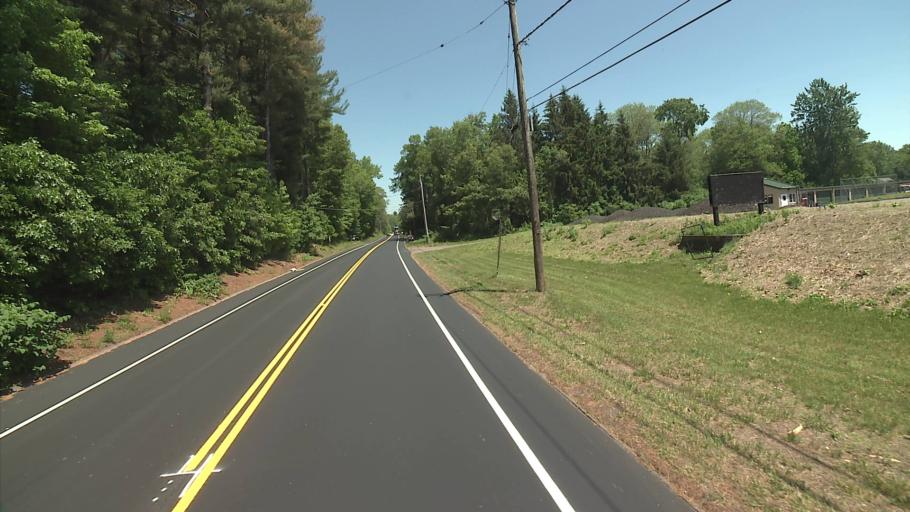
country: US
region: Connecticut
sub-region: Tolland County
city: Crystal Lake
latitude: 41.9341
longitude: -72.3818
